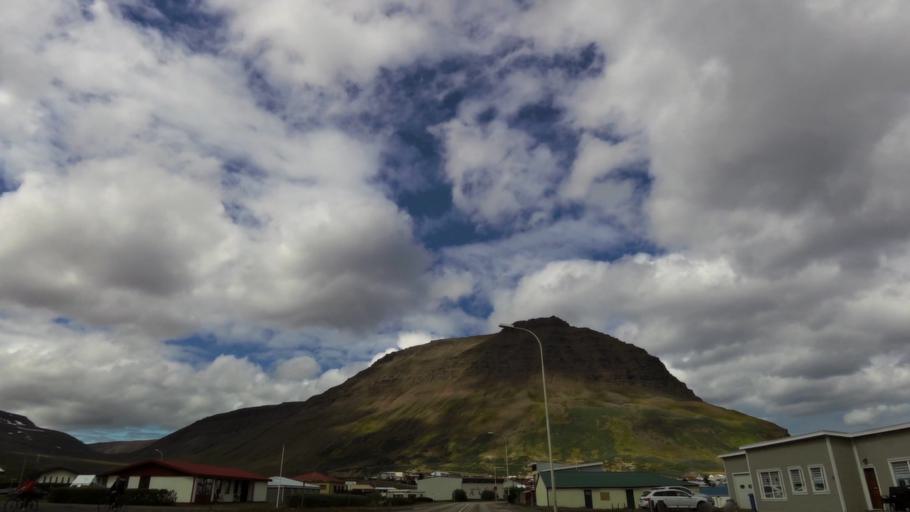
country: IS
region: Westfjords
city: Isafjoerdur
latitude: 66.1534
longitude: -23.2497
